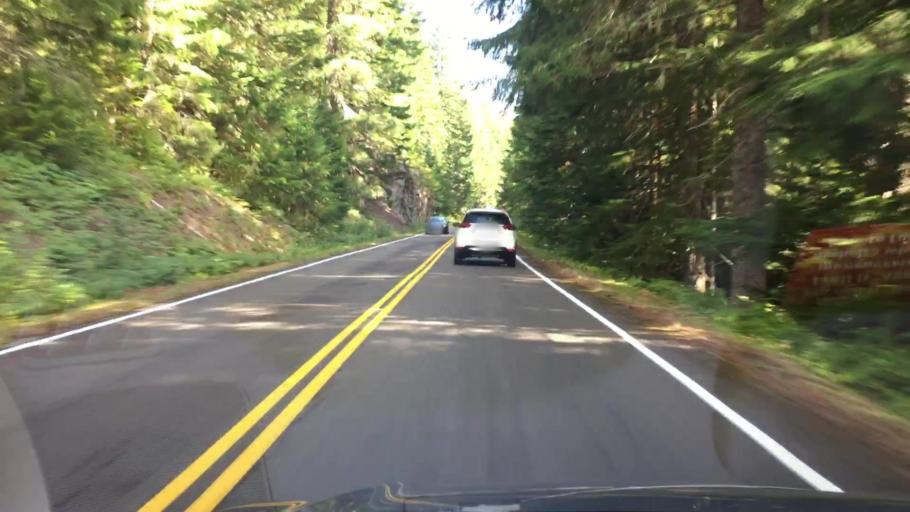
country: US
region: Washington
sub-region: Pierce County
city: Buckley
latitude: 46.7319
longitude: -121.6119
